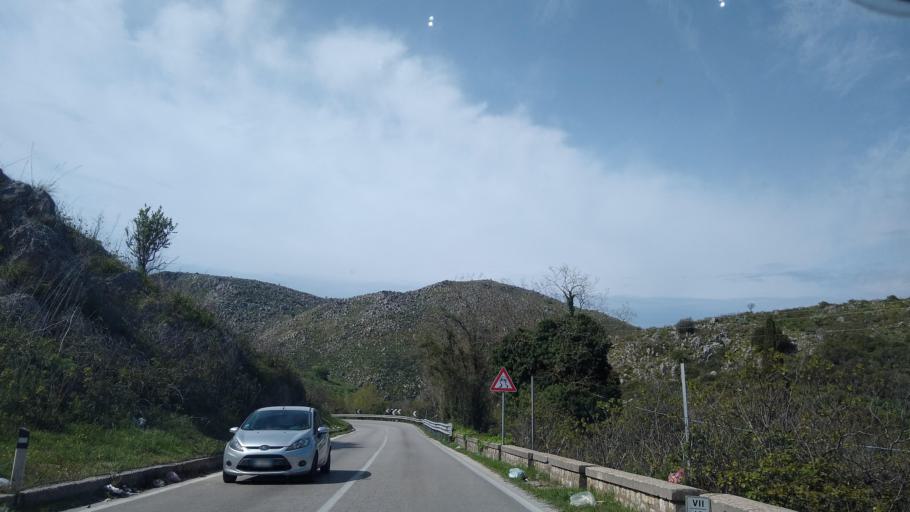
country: IT
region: Sicily
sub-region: Palermo
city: Pioppo
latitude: 38.0449
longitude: 13.1989
